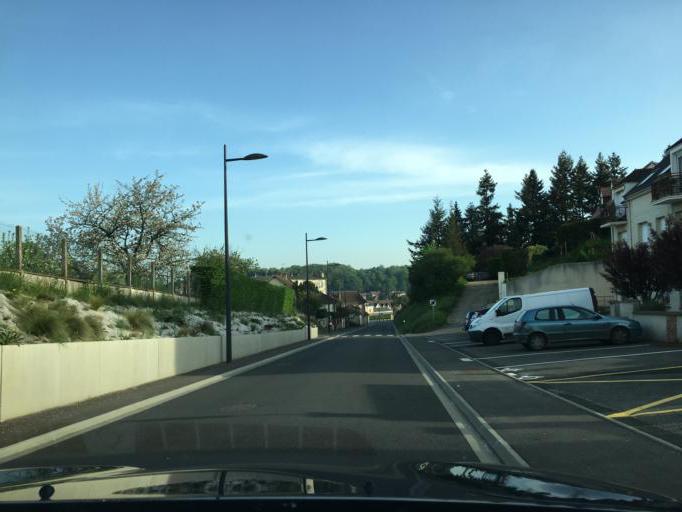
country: FR
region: Centre
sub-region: Departement d'Eure-et-Loir
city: Epernon
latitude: 48.6025
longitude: 1.6819
